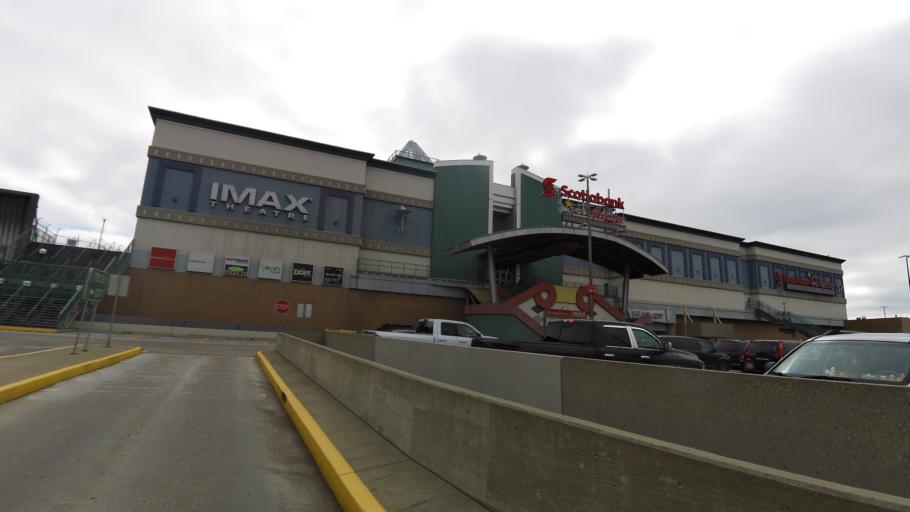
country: CA
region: Alberta
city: St. Albert
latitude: 53.5231
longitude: -113.6294
